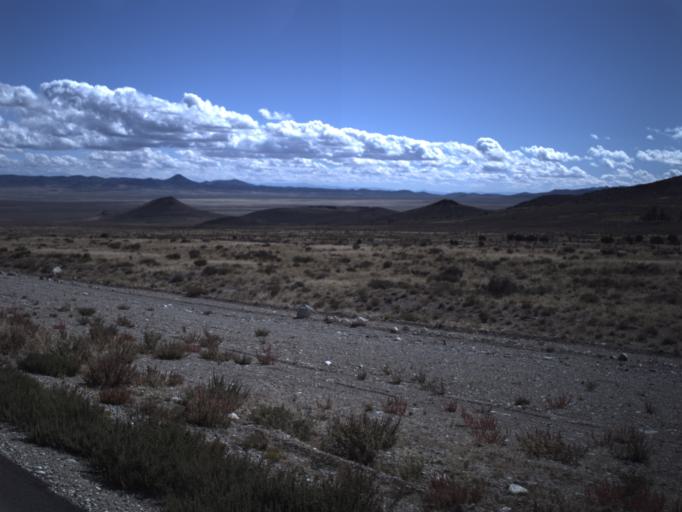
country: US
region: Utah
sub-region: Beaver County
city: Milford
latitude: 38.5003
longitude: -113.4986
